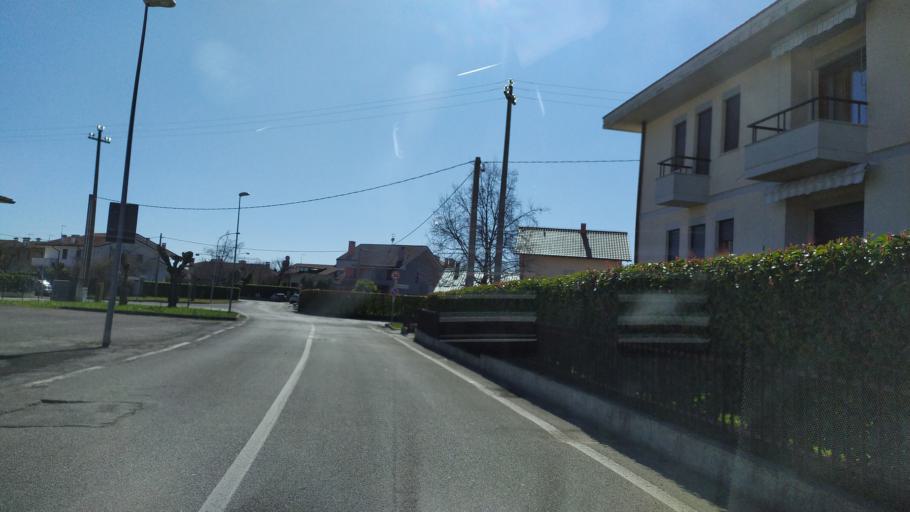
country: IT
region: Veneto
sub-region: Provincia di Vicenza
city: Breganze
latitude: 45.7013
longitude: 11.5665
